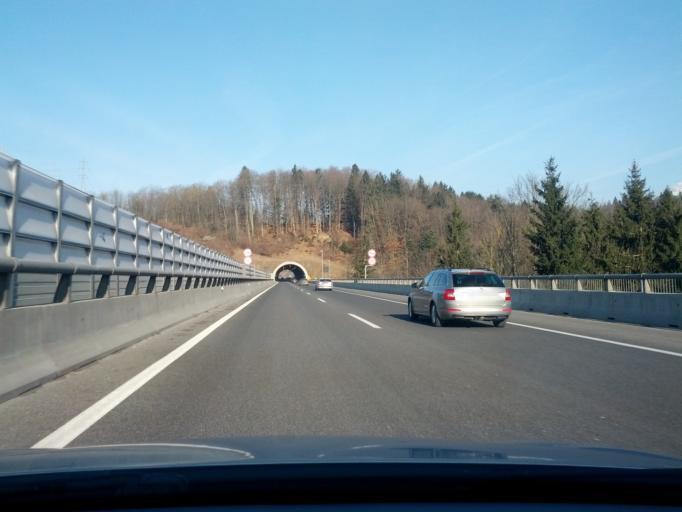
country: SI
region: Trzic
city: Bistrica pri Trzicu
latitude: 46.3161
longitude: 14.2492
